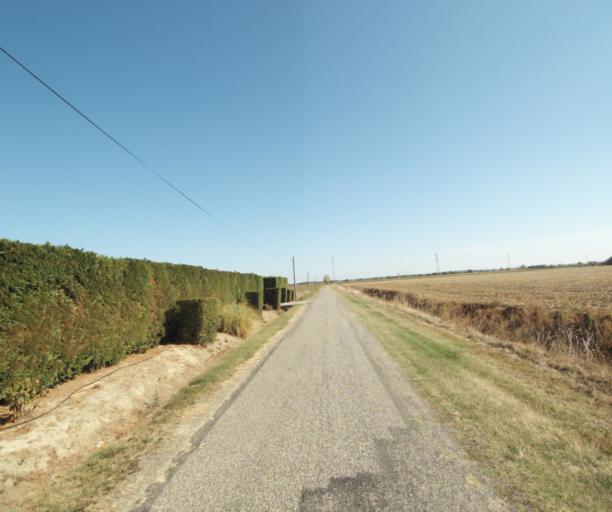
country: FR
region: Midi-Pyrenees
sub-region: Departement du Tarn-et-Garonne
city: Verdun-sur-Garonne
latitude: 43.8336
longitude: 1.2123
